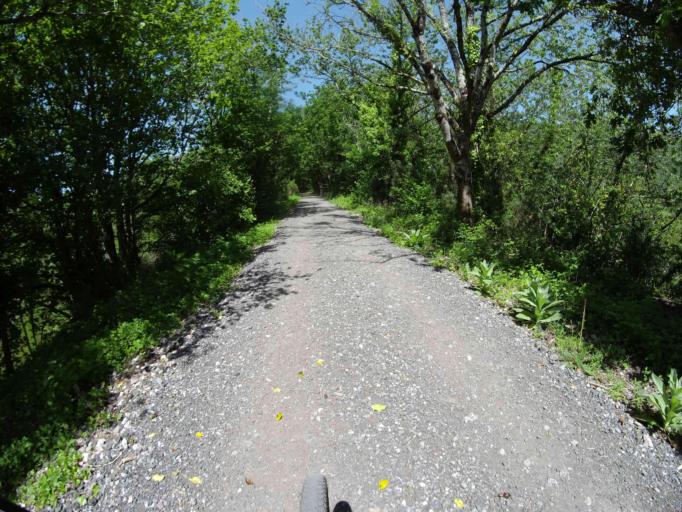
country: GB
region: England
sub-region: Devon
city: Bovey Tracey
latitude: 50.6233
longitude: -3.7155
